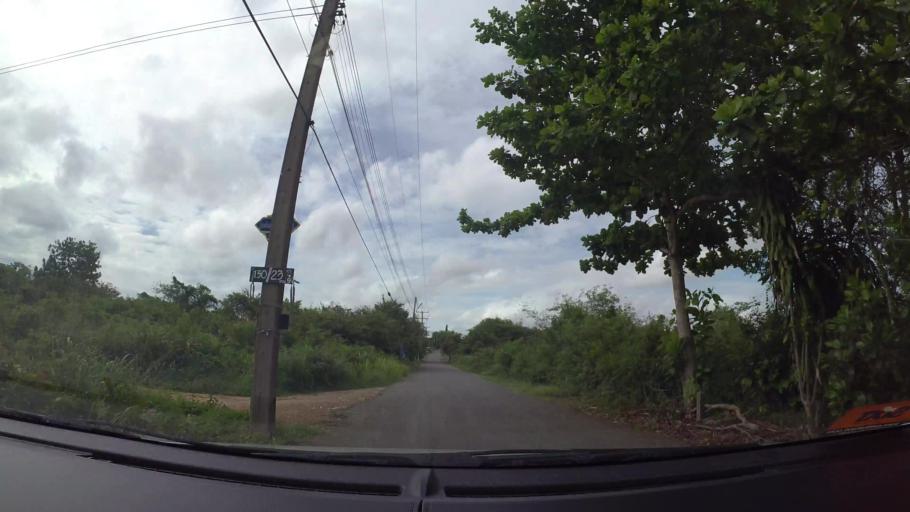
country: TH
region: Chon Buri
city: Sattahip
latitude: 12.7192
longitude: 100.8995
